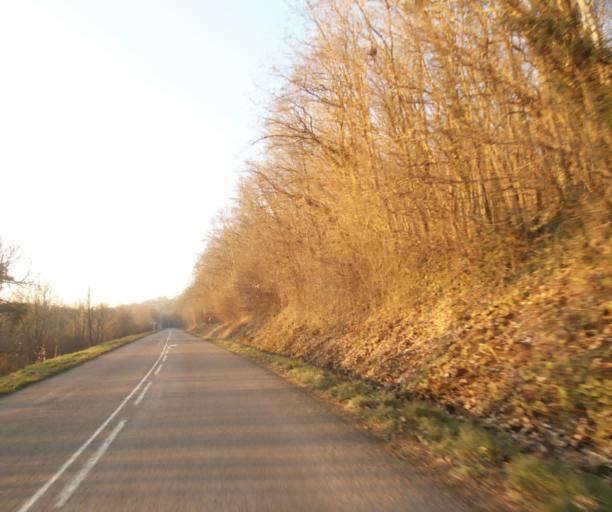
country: FR
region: Lorraine
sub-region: Departement de la Meuse
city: Ancerville
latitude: 48.6118
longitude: 5.0462
